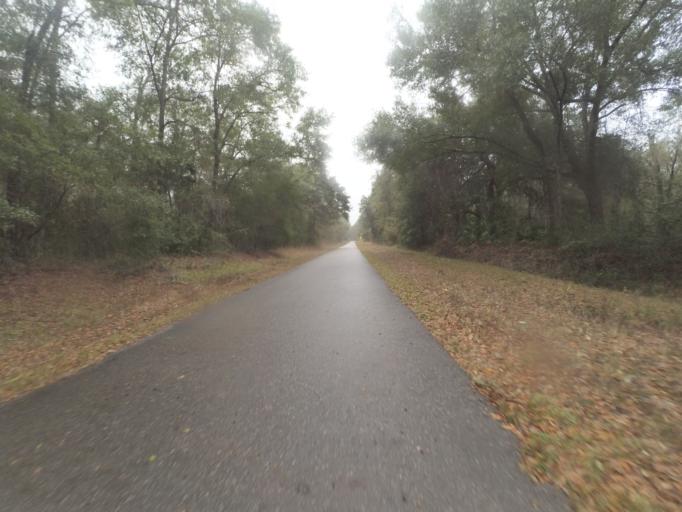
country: US
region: Florida
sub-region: Alachua County
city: Hawthorne
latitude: 29.5914
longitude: -82.1294
